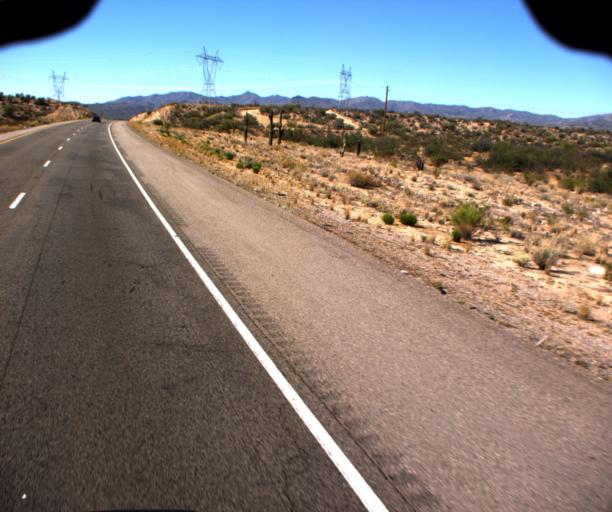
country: US
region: Arizona
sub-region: Yavapai County
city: Bagdad
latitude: 34.7534
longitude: -113.6163
